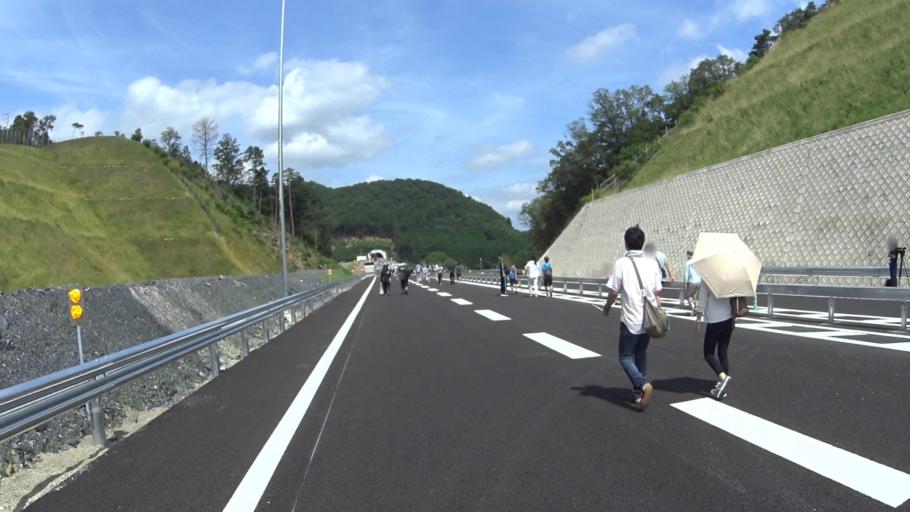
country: JP
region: Hyogo
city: Sasayama
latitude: 35.1562
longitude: 135.4111
